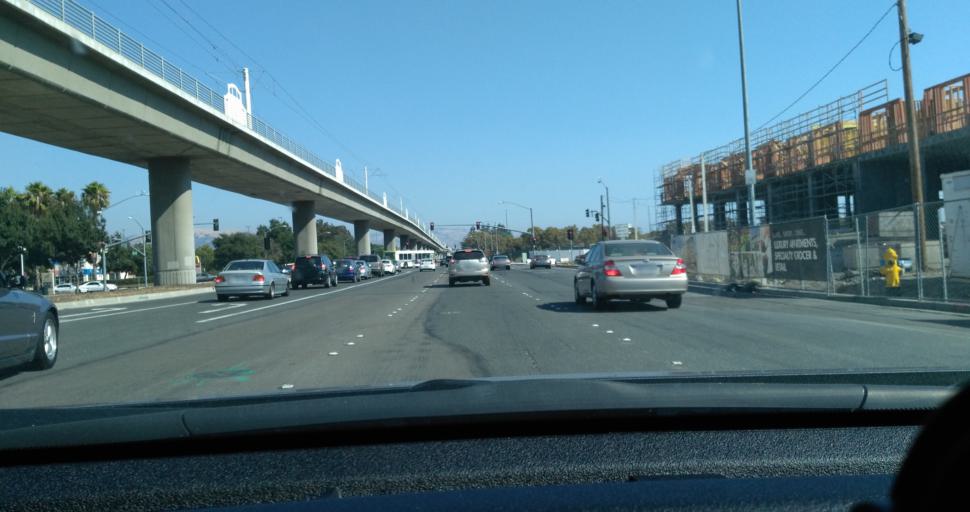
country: US
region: California
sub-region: Santa Clara County
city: Milpitas
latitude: 37.4129
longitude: -121.9000
